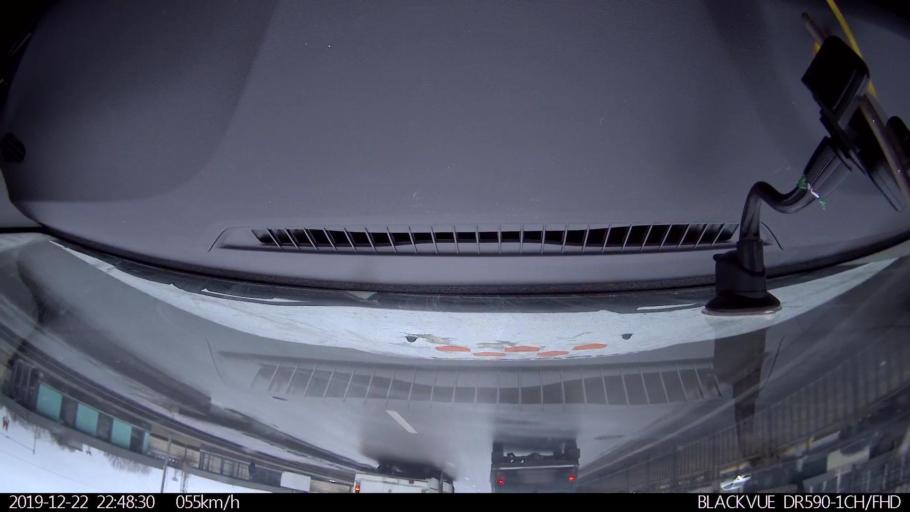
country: RU
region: Nizjnij Novgorod
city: Nizhniy Novgorod
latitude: 56.2525
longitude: 43.8892
